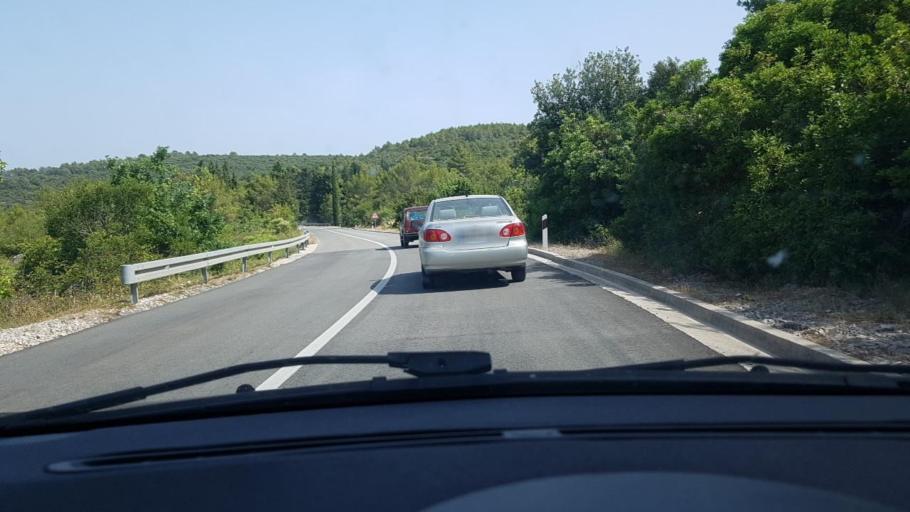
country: HR
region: Dubrovacko-Neretvanska
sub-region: Grad Korcula
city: Zrnovo
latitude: 42.9377
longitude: 17.0792
